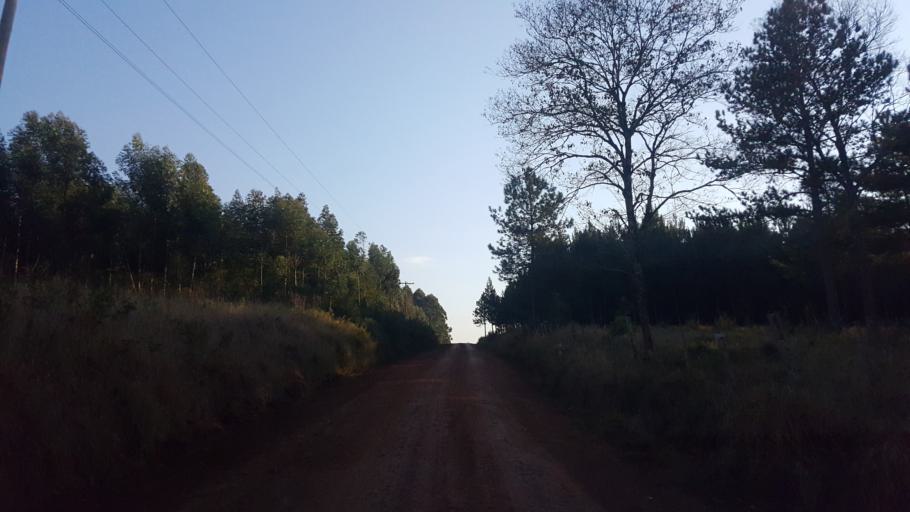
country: AR
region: Misiones
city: Capiovi
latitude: -26.9179
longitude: -55.0516
